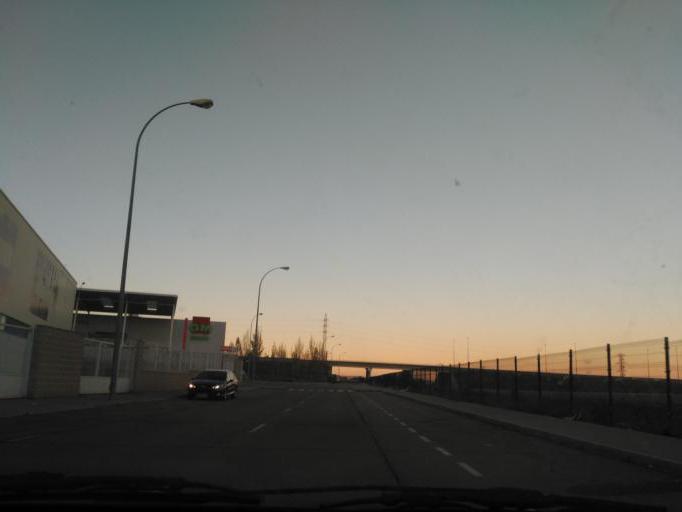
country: ES
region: Castille and Leon
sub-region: Provincia de Salamanca
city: Carbajosa de la Sagrada
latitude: 40.9408
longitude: -5.6518
